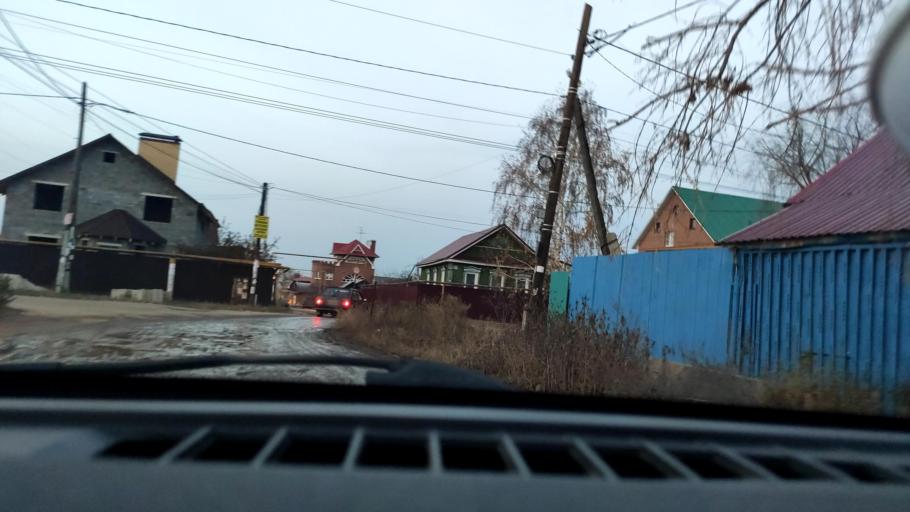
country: RU
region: Samara
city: Samara
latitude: 53.1350
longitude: 50.0950
